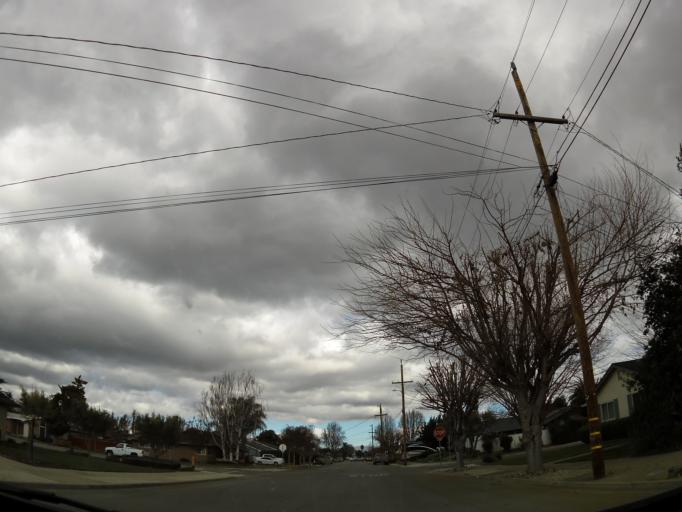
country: US
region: California
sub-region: San Benito County
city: Hollister
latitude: 36.8359
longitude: -121.3994
